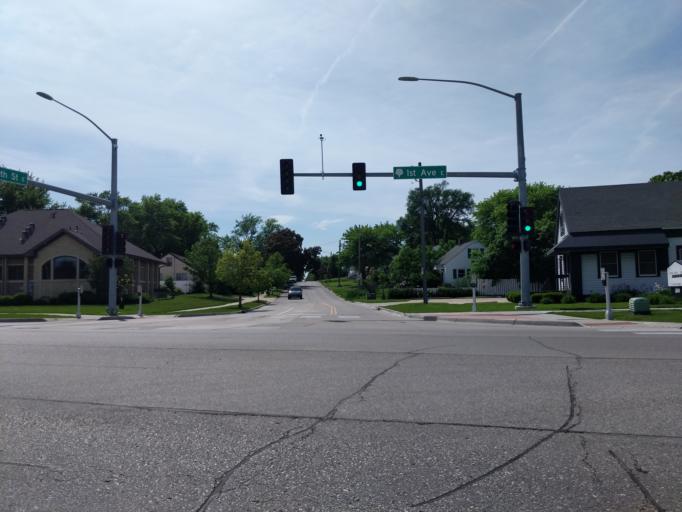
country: US
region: Iowa
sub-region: Linn County
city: Cedar Rapids
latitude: 42.0170
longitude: -91.6344
